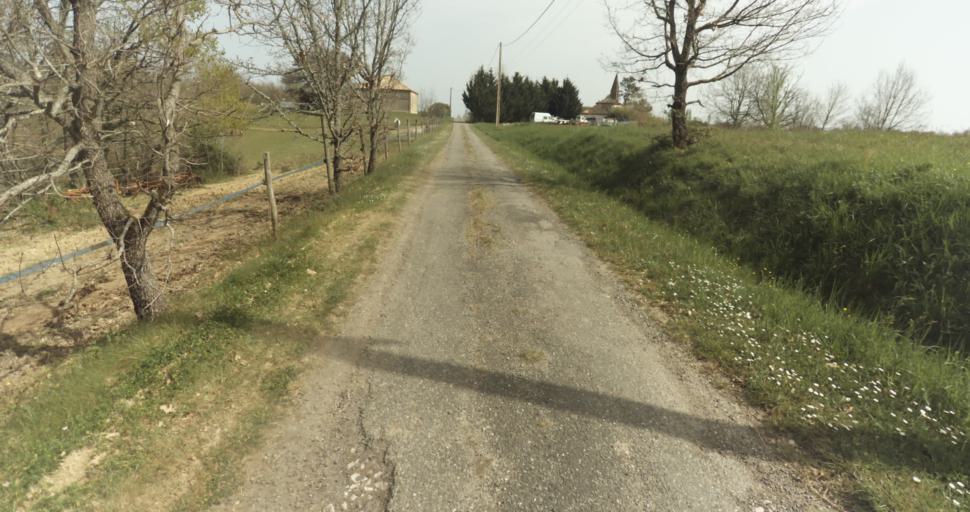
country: FR
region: Midi-Pyrenees
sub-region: Departement du Tarn-et-Garonne
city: Moissac
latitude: 44.1485
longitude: 1.1387
